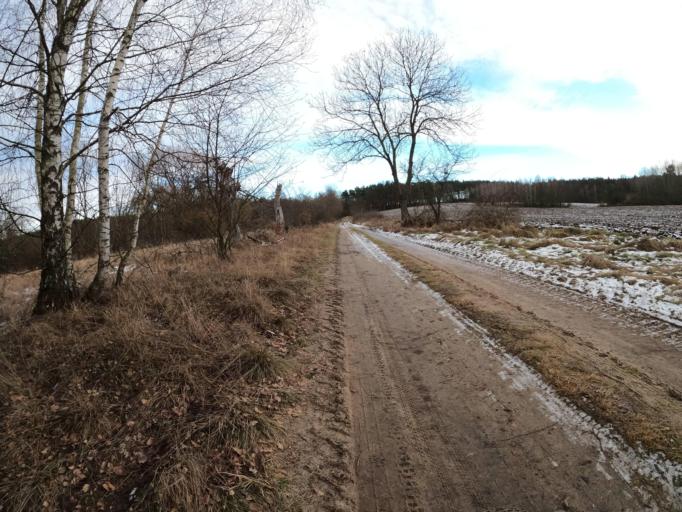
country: PL
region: Lubusz
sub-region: Powiat slubicki
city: Cybinka
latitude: 52.2049
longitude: 14.8500
